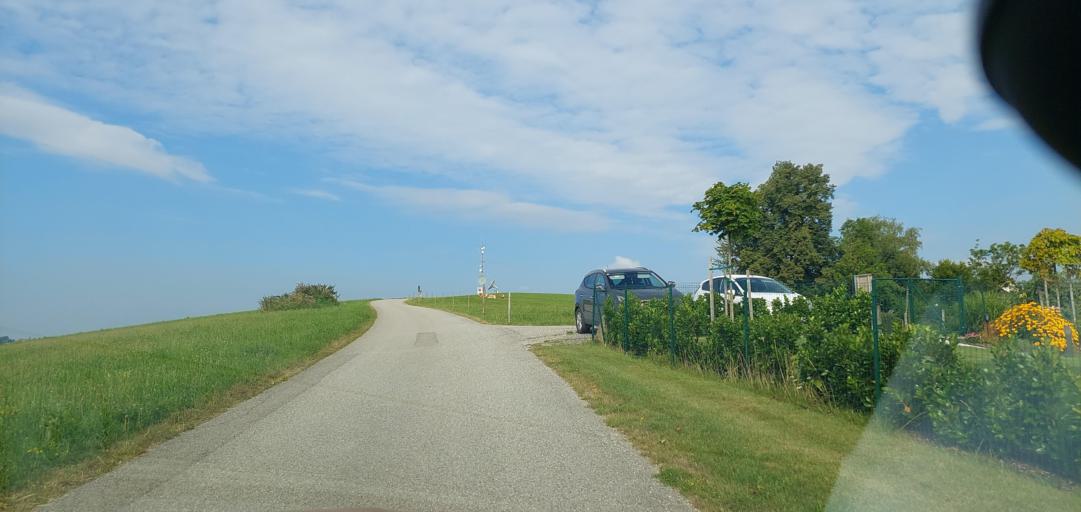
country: AT
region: Upper Austria
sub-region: Politischer Bezirk Urfahr-Umgebung
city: Feldkirchen an der Donau
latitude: 48.3313
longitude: 13.9816
